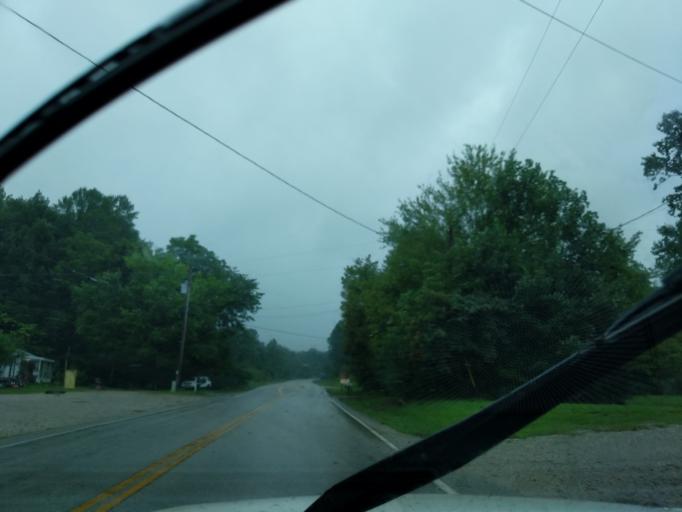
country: US
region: Kentucky
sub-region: Barren County
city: Cave City
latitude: 37.1282
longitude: -86.0613
